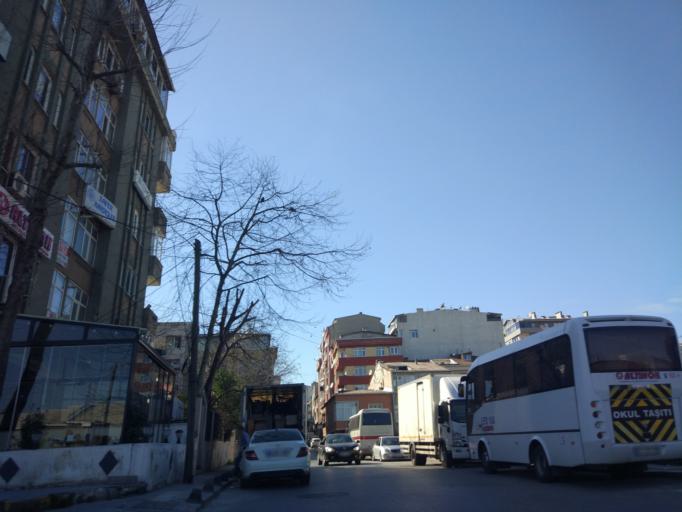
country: TR
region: Istanbul
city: Mahmutbey
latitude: 41.0238
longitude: 28.8061
